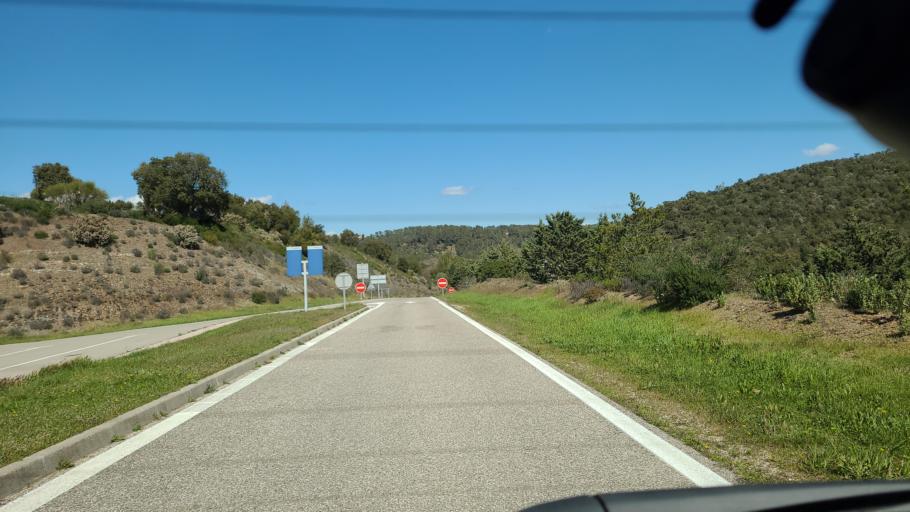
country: FR
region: Provence-Alpes-Cote d'Azur
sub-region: Departement du Var
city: Carnoules
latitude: 43.2834
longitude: 6.1880
